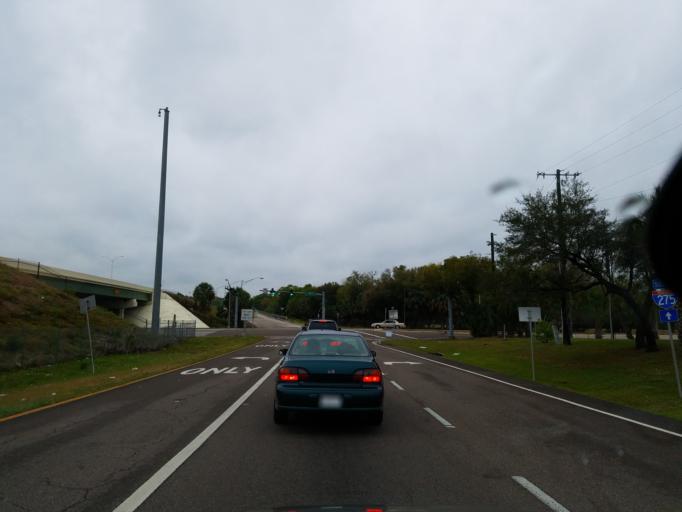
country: US
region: Florida
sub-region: Hillsborough County
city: Carrollwood
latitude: 28.0233
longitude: -82.4564
